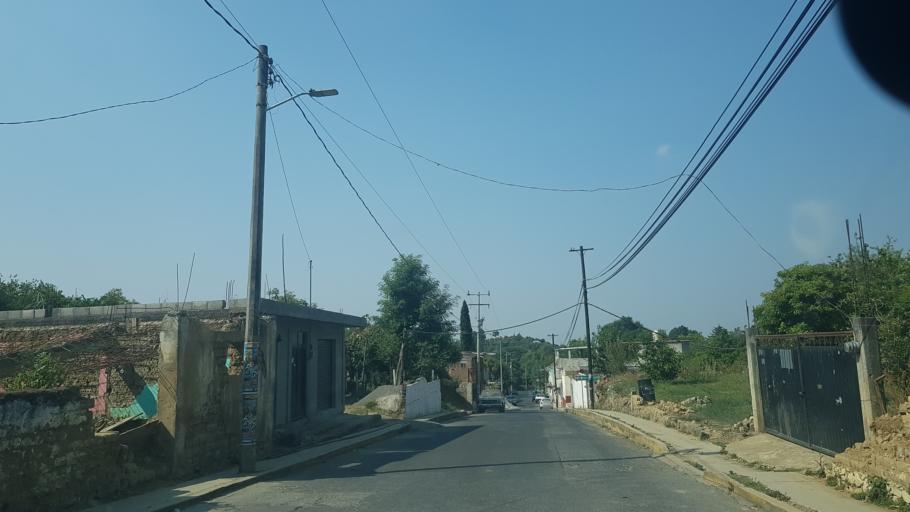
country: MX
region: Morelos
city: Hueyapan
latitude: 18.8824
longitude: -98.6919
